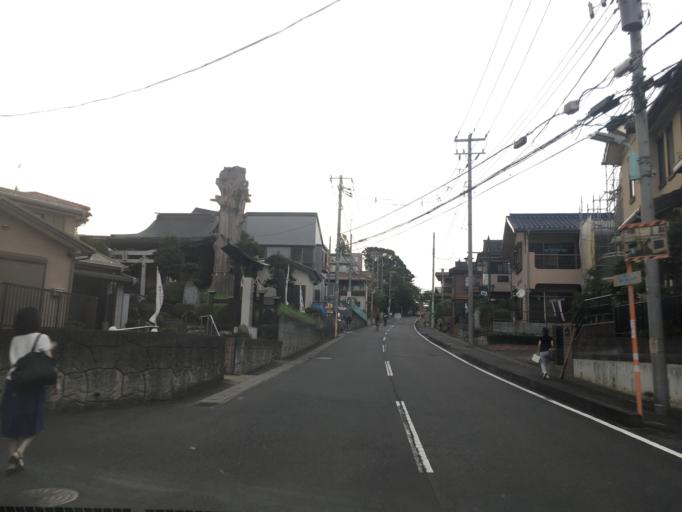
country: JP
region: Saitama
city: Tokorozawa
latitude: 35.7832
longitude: 139.4400
